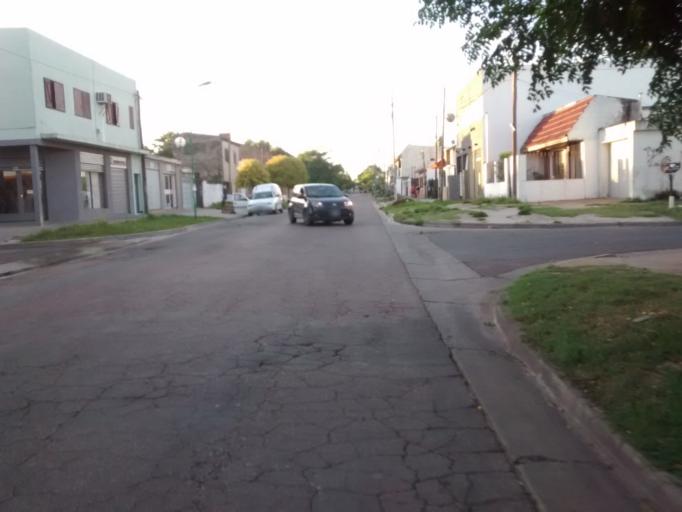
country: AR
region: Buenos Aires
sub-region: Partido de La Plata
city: La Plata
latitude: -34.9489
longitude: -57.9382
